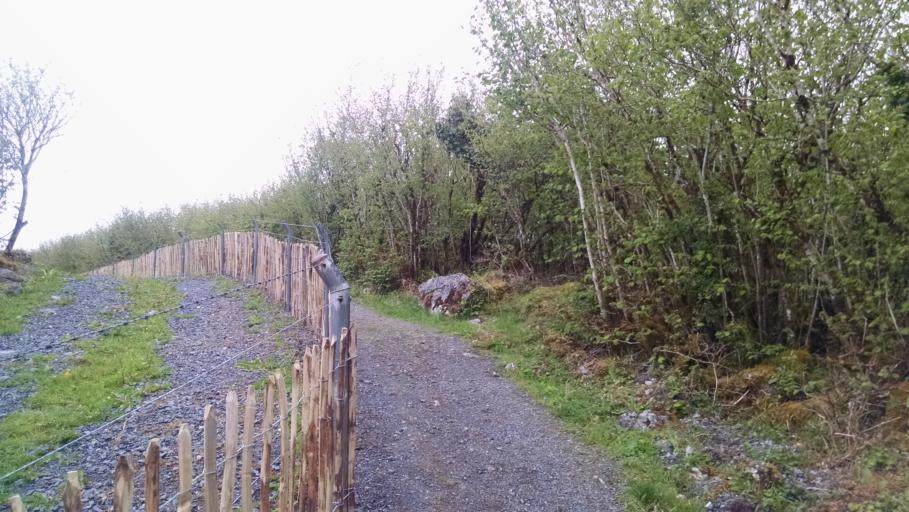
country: IE
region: Munster
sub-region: An Clar
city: Ennis
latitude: 53.0116
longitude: -9.0752
